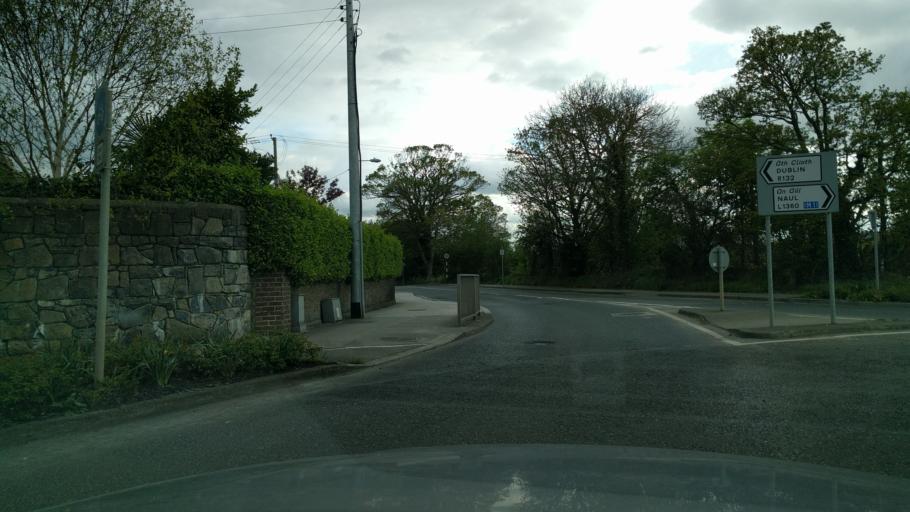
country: IE
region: Leinster
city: Balbriggan
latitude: 53.6032
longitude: -6.1845
